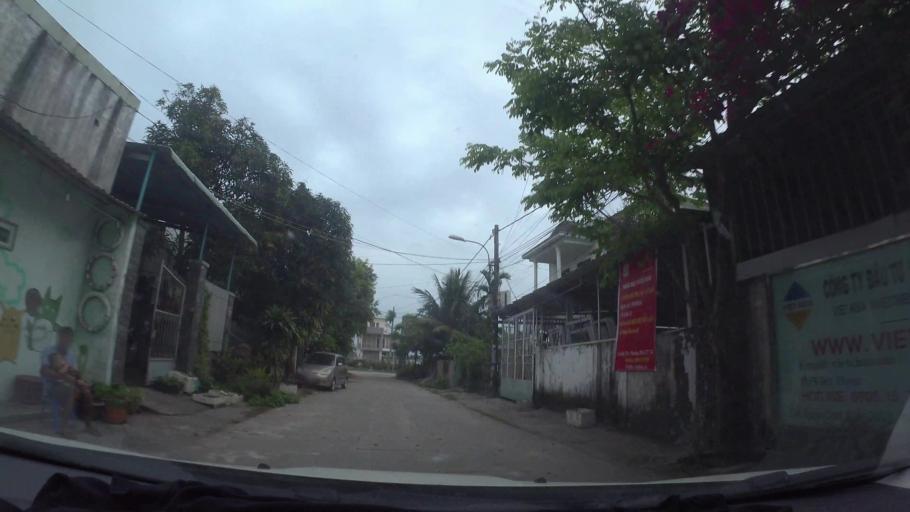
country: VN
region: Da Nang
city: Lien Chieu
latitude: 16.0871
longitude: 108.1543
